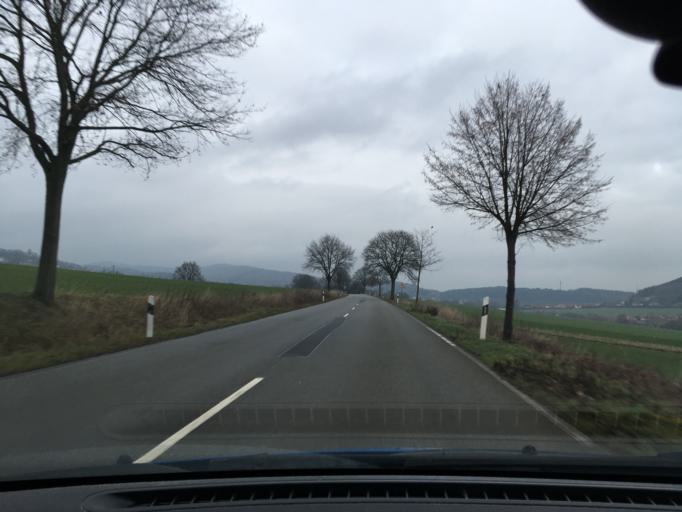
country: DE
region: Lower Saxony
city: Hardegsen
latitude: 51.6388
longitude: 9.8146
